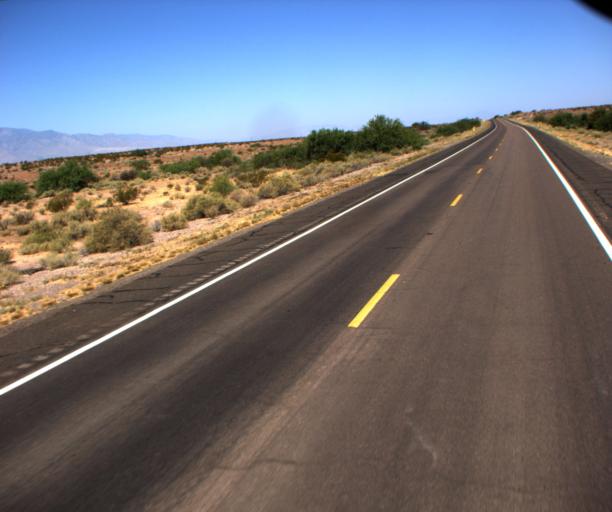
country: US
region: Arizona
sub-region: Graham County
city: Safford
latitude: 32.7973
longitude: -109.5604
